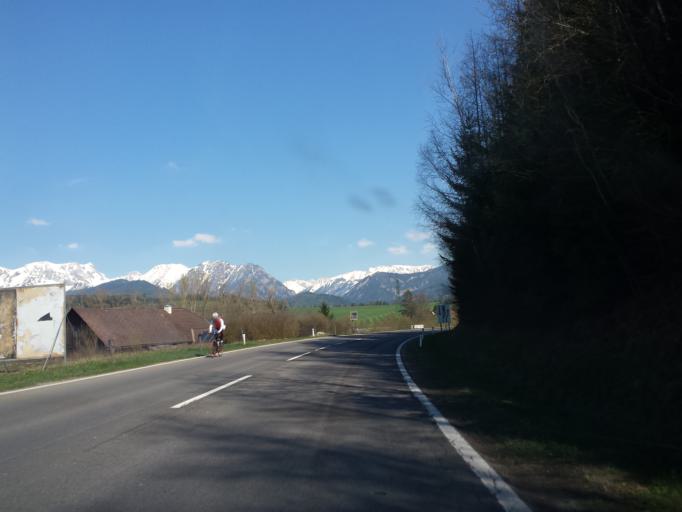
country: AT
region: Styria
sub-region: Politischer Bezirk Leoben
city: Trofaiach
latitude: 47.4013
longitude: 14.9942
